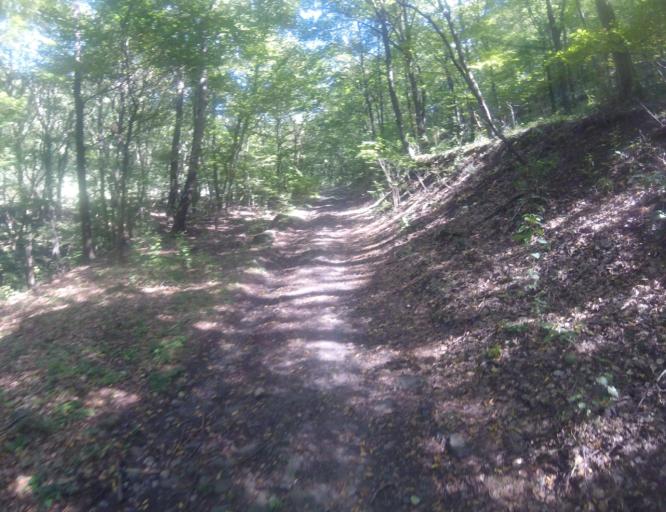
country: HU
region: Nograd
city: Bujak
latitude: 47.9387
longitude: 19.6054
